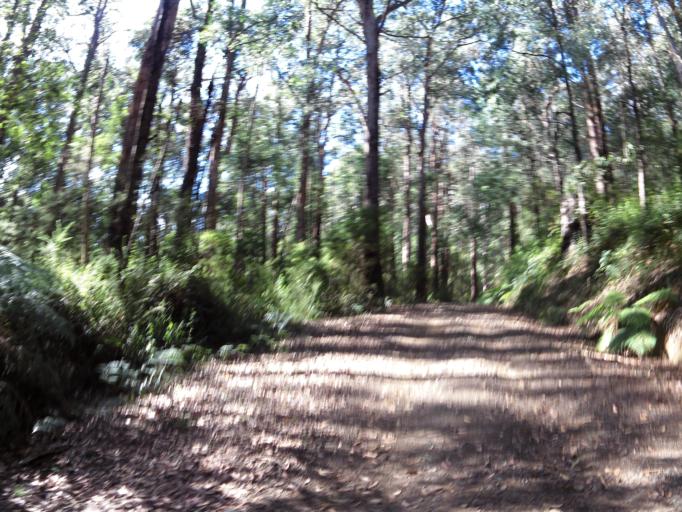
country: AU
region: Victoria
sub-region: Yarra Ranges
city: Millgrove
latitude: -37.8533
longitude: 145.7818
